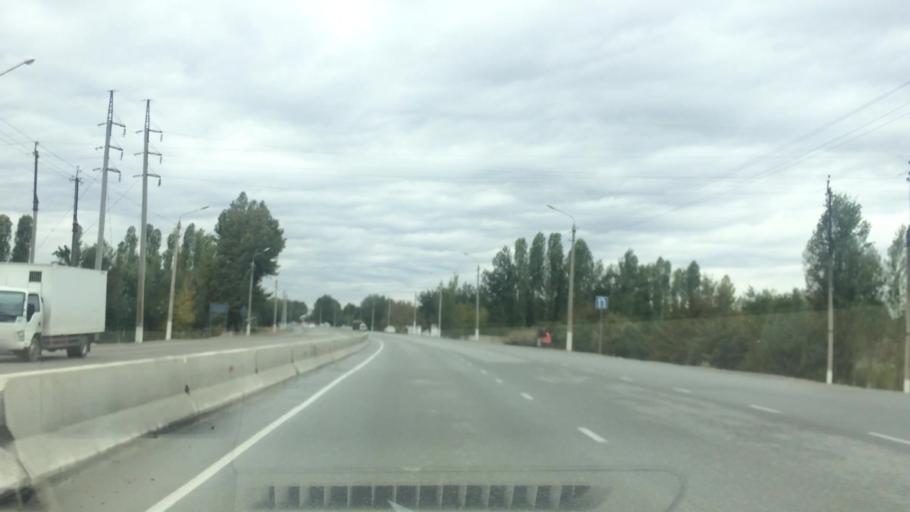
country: UZ
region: Jizzax
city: Jizzax
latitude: 39.9885
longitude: 67.5798
